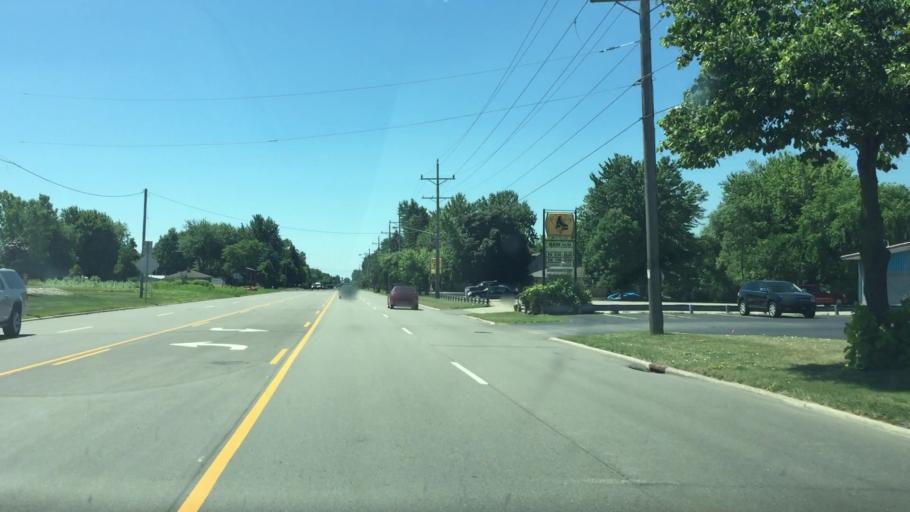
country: US
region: Wisconsin
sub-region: Outagamie County
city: Appleton
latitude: 44.2272
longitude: -88.4041
